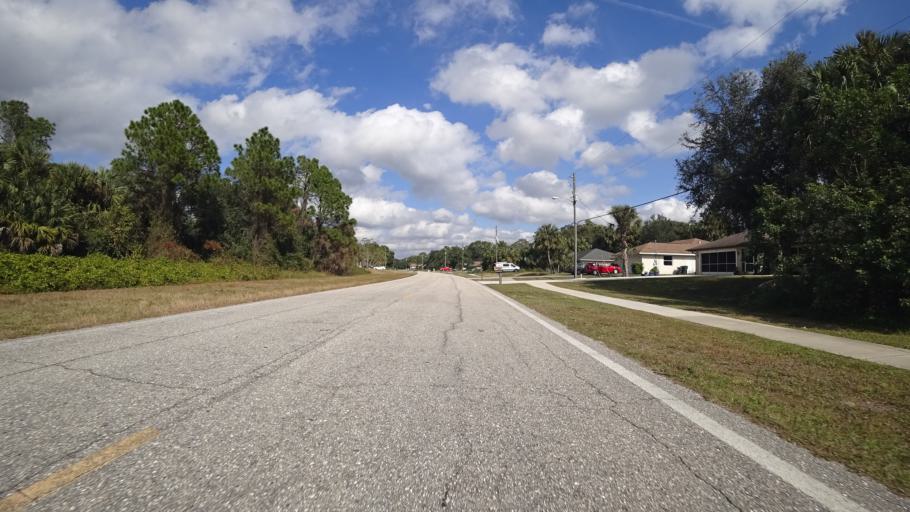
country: US
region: Florida
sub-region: Charlotte County
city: Port Charlotte
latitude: 27.0520
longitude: -82.1176
